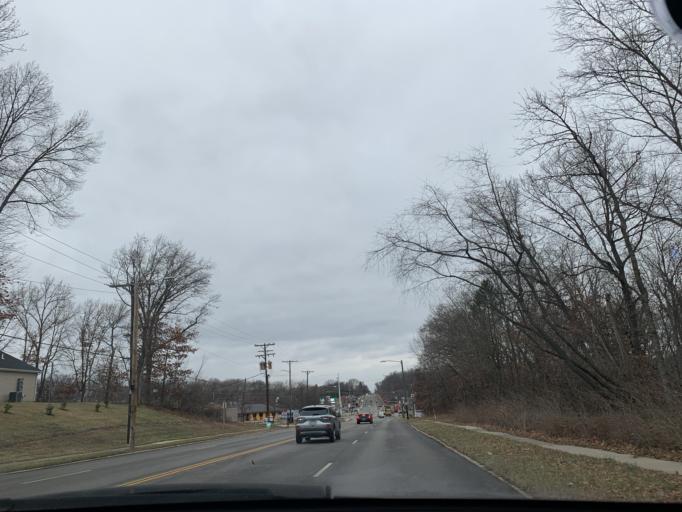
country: US
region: Illinois
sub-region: Sangamon County
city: Leland Grove
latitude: 39.7970
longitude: -89.6870
